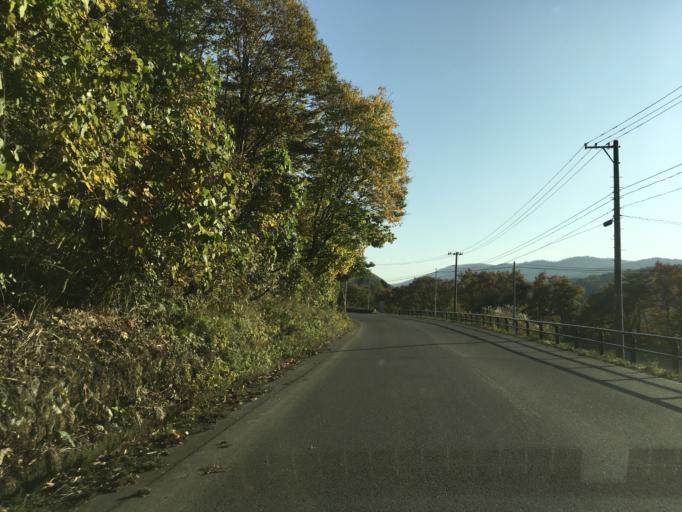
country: JP
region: Akita
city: Yuzawa
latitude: 39.1059
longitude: 140.7213
